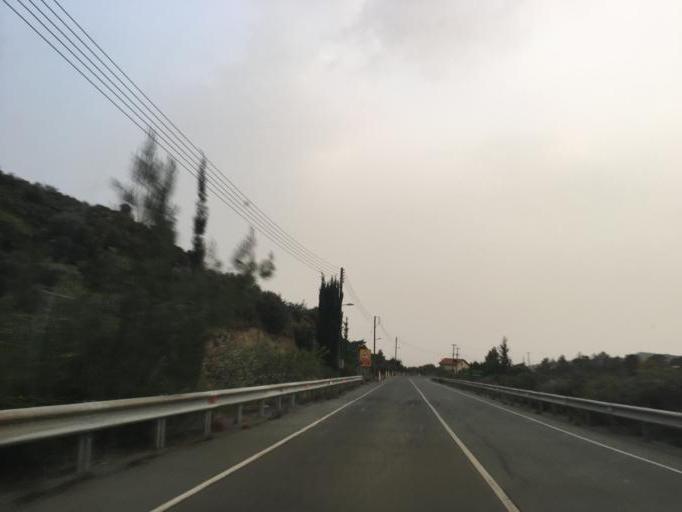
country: CY
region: Limassol
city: Parekklisha
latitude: 34.8099
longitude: 33.1515
